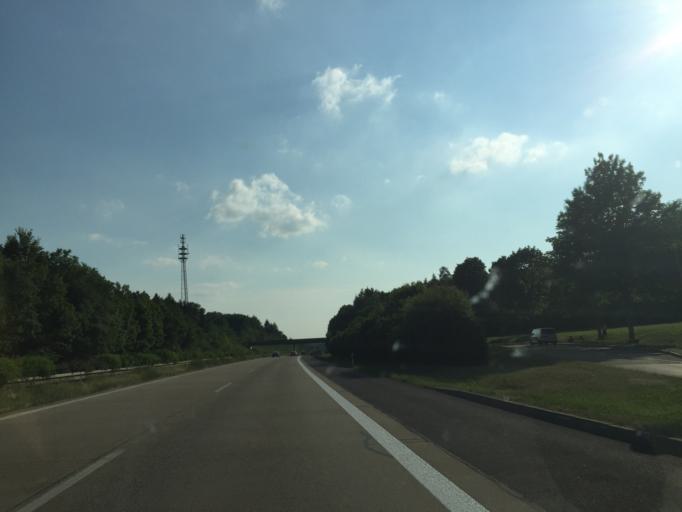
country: DE
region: Baden-Wuerttemberg
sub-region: Karlsruhe Region
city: Rosenberg
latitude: 49.4325
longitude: 9.5049
